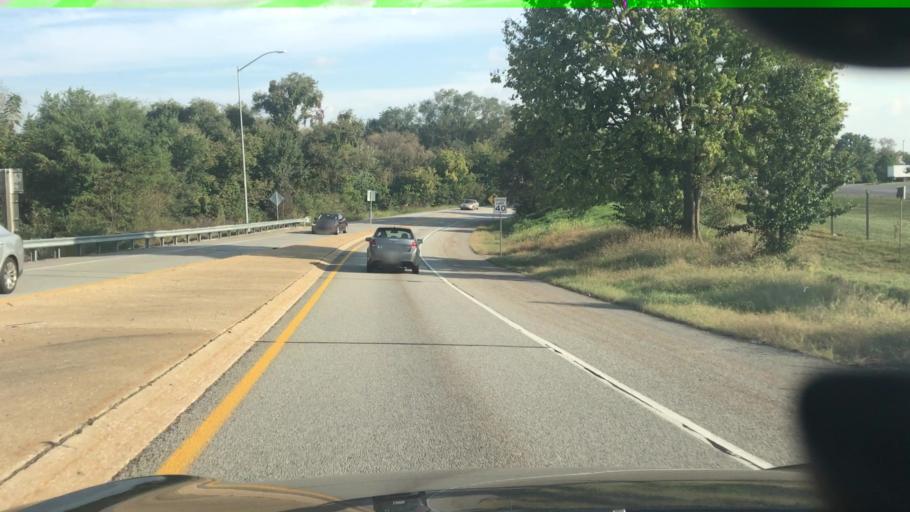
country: US
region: Pennsylvania
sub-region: Cumberland County
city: Shiremanstown
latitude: 40.2142
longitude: -76.9461
